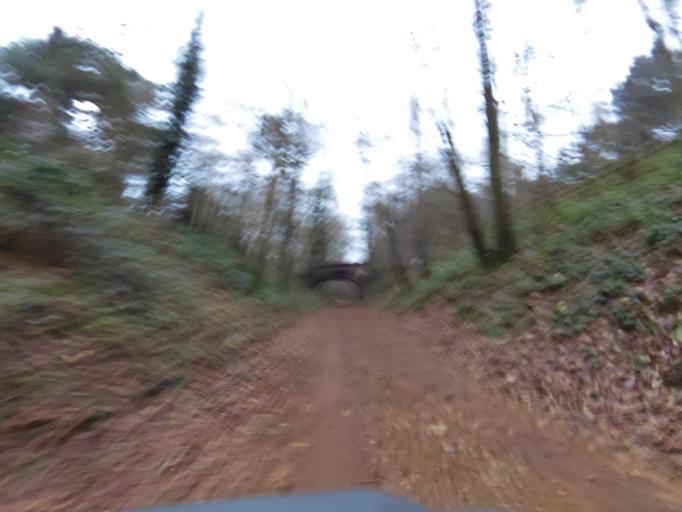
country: GB
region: England
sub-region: Norfolk
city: Costessey
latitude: 52.7087
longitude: 1.1726
